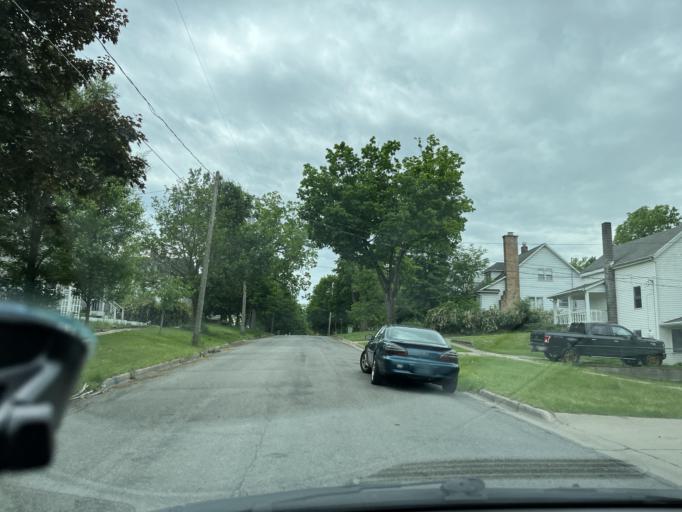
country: US
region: Michigan
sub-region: Barry County
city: Hastings
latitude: 42.6477
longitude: -85.2937
